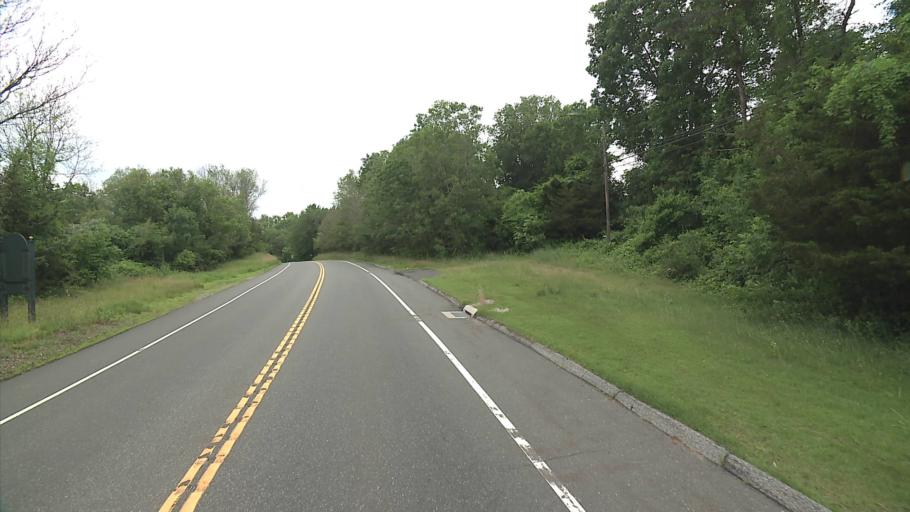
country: US
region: Connecticut
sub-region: New London County
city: Ledyard Center
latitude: 41.4830
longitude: -72.0324
